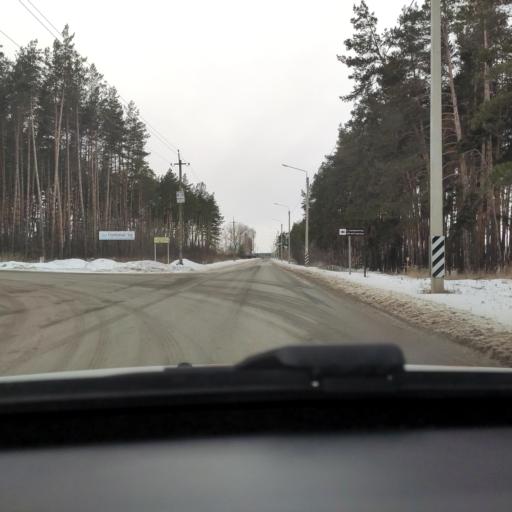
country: RU
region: Voronezj
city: Ramon'
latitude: 51.9380
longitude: 39.2134
